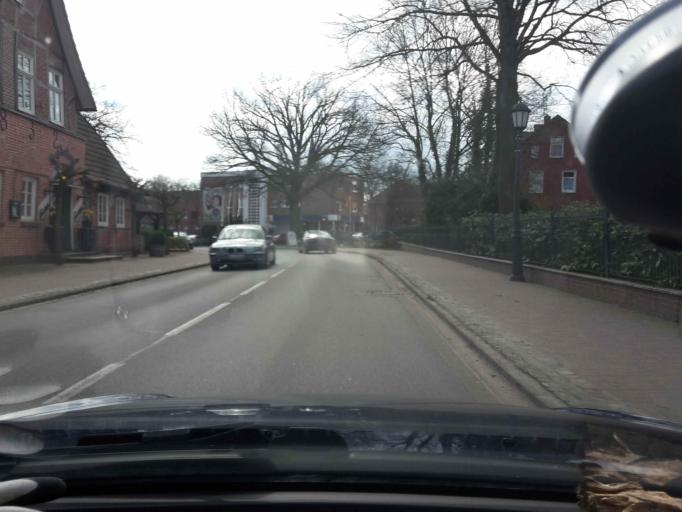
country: DE
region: Lower Saxony
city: Hanstedt
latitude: 53.2598
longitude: 10.0129
